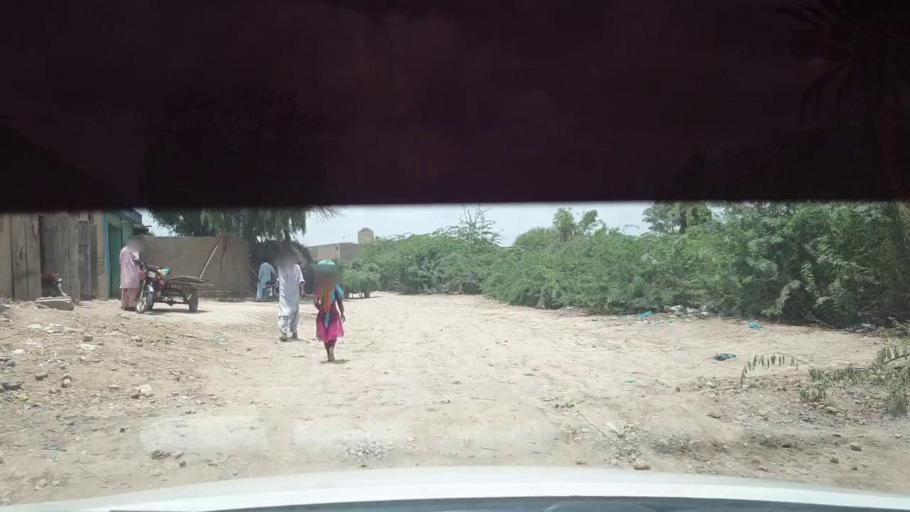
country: PK
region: Sindh
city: Kadhan
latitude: 24.4818
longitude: 68.9910
